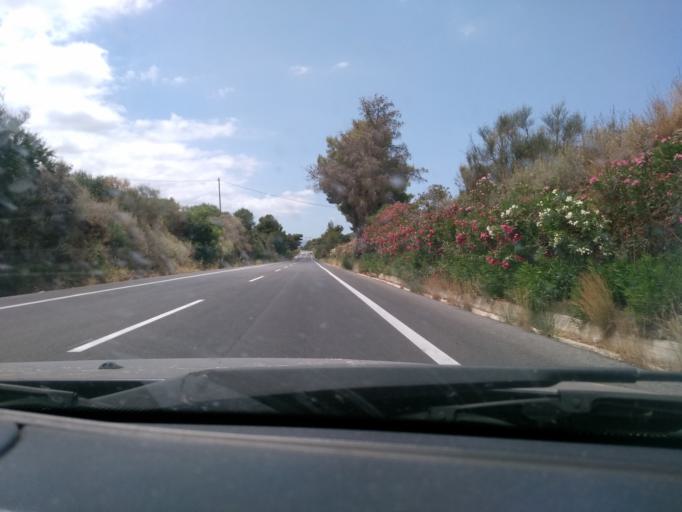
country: GR
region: Crete
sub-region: Nomos Chanias
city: Georgioupolis
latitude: 35.3641
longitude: 24.2382
